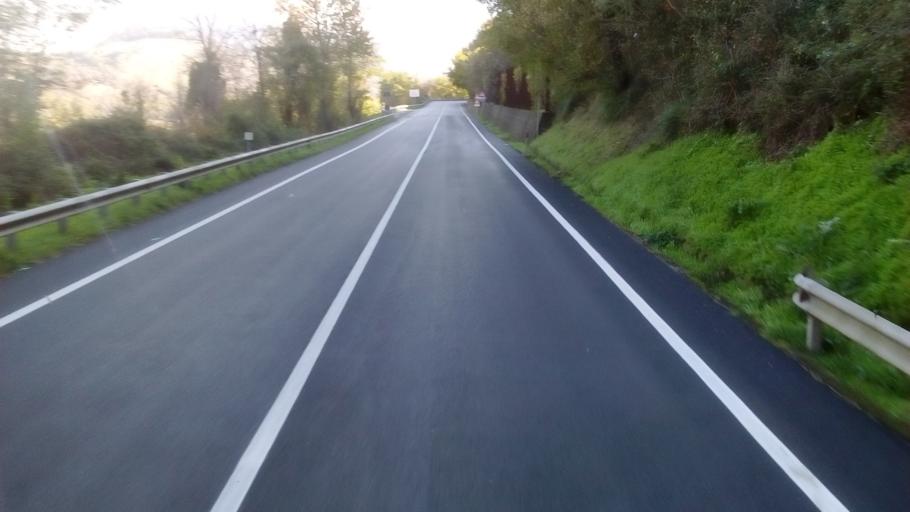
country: IT
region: Molise
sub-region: Provincia di Isernia
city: Conca Casale
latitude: 41.4574
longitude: 14.0128
